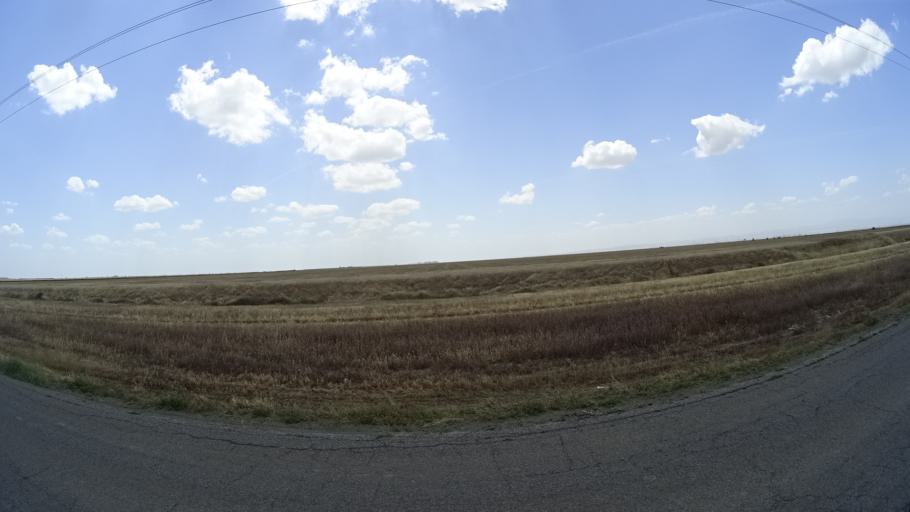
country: US
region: California
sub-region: Kings County
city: Stratford
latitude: 36.1893
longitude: -119.8910
